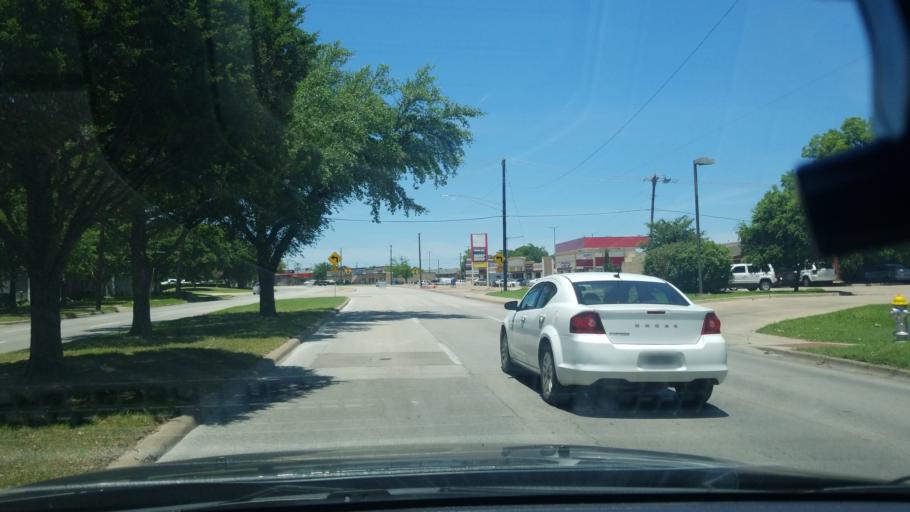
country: US
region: Texas
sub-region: Dallas County
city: Mesquite
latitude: 32.7812
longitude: -96.6006
